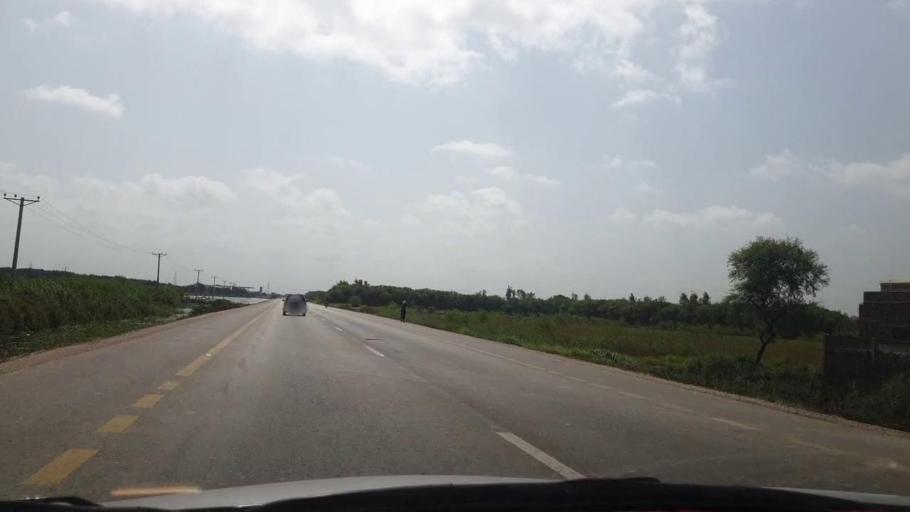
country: PK
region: Sindh
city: Talhar
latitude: 24.9348
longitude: 68.7095
